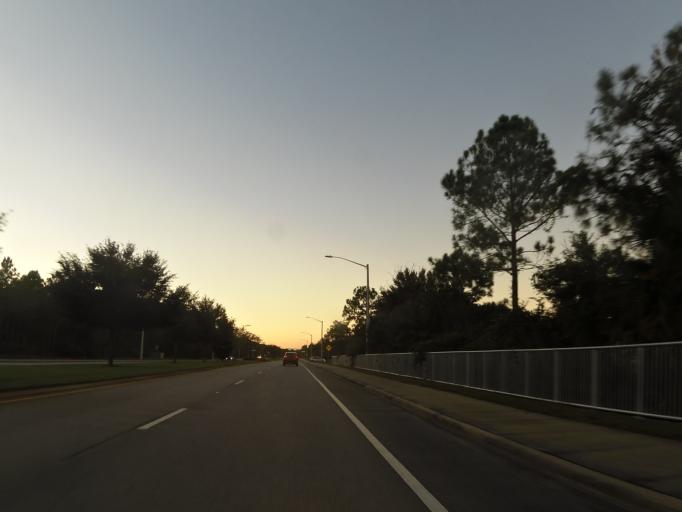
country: US
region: Florida
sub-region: Flagler County
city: Palm Coast
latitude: 29.5869
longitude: -81.2587
